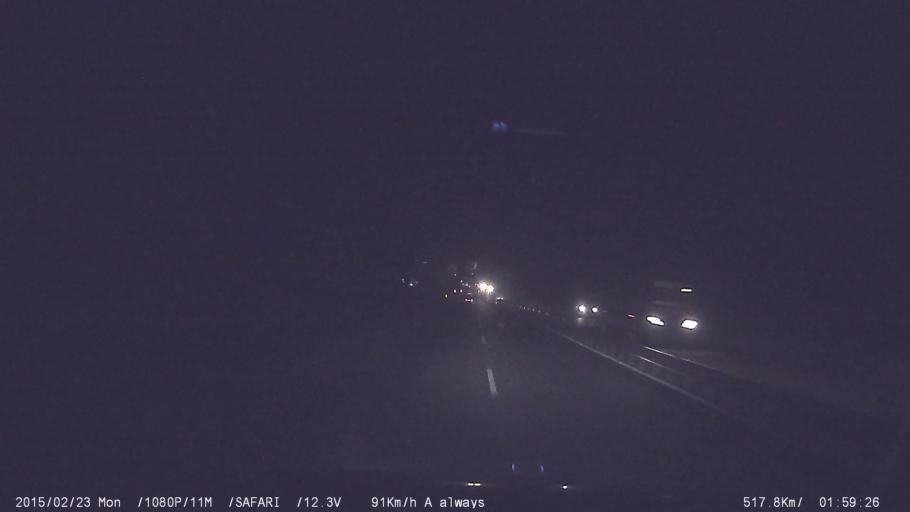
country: IN
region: Tamil Nadu
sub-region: Krishnagiri
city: Krishnagiri
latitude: 12.6138
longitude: 78.0888
